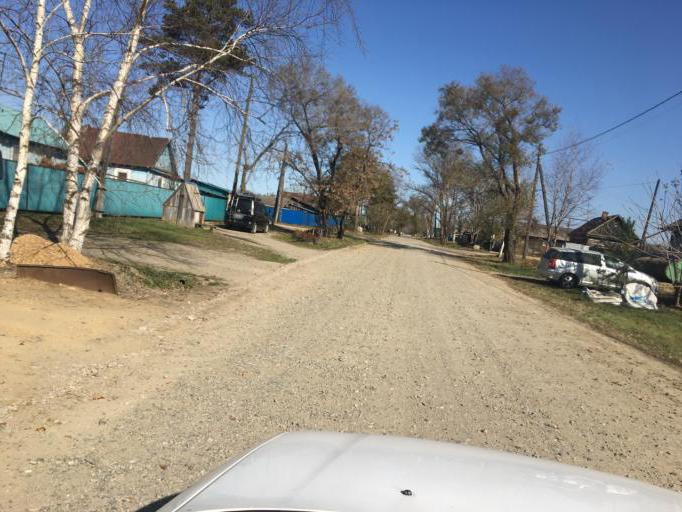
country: RU
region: Primorskiy
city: Dal'nerechensk
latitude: 45.9257
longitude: 133.7467
